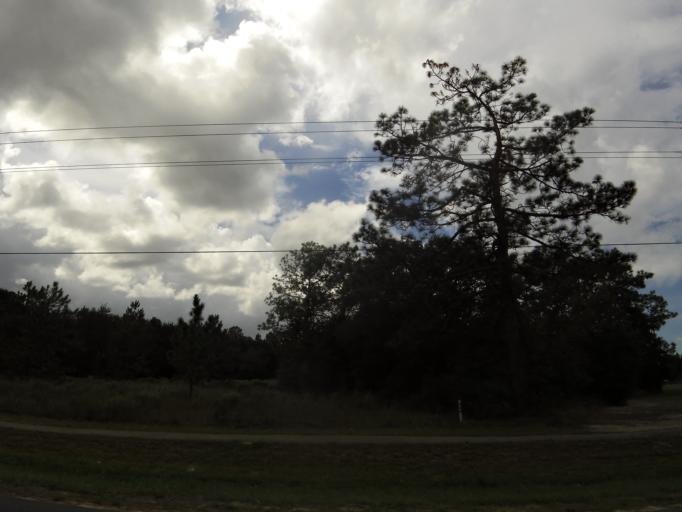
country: US
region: Florida
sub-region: Clay County
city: Middleburg
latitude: 30.0859
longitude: -81.9430
